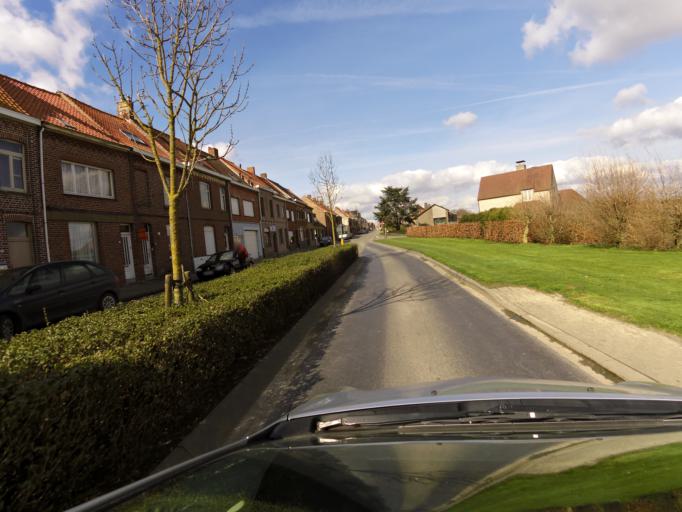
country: FR
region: Nord-Pas-de-Calais
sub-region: Departement du Nord
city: Nieppe
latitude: 50.7420
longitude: 2.8211
